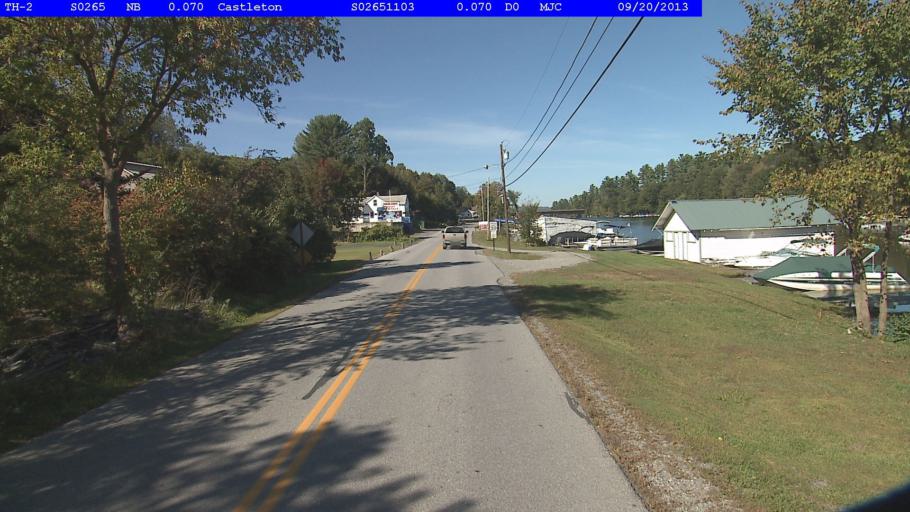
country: US
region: Vermont
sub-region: Rutland County
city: Fair Haven
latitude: 43.6057
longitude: -73.2336
